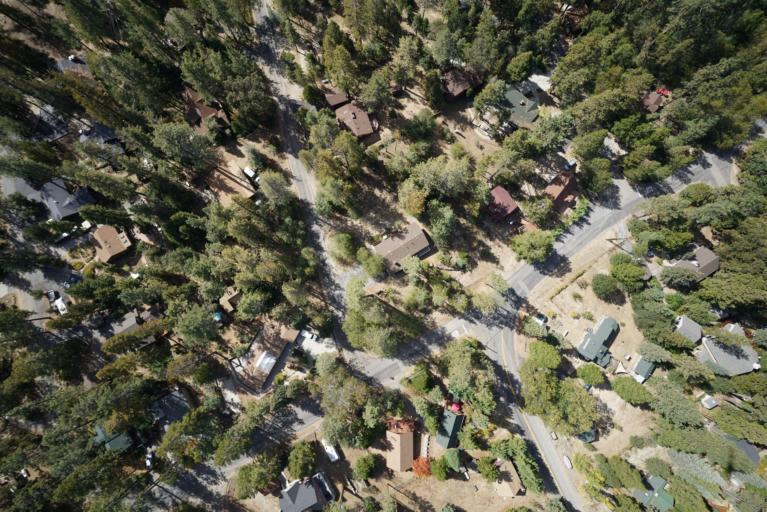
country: US
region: California
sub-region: Riverside County
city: Idyllwild
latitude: 33.7535
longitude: -116.7015
